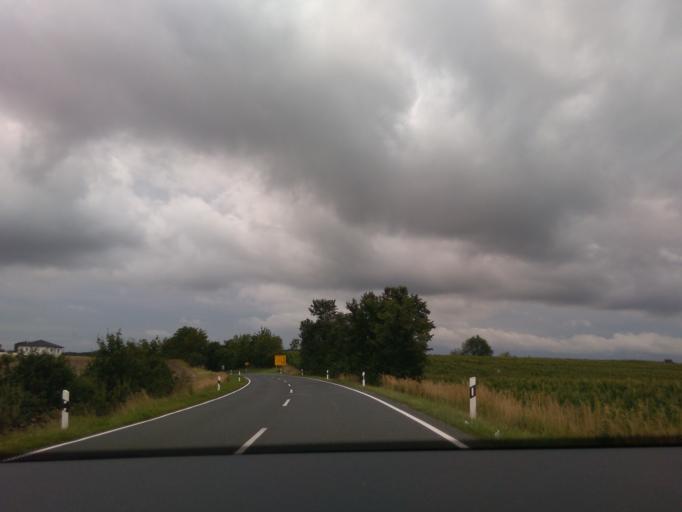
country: DE
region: Bavaria
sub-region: Regierungsbezirk Mittelfranken
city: Weisendorf
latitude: 49.6274
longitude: 10.8237
